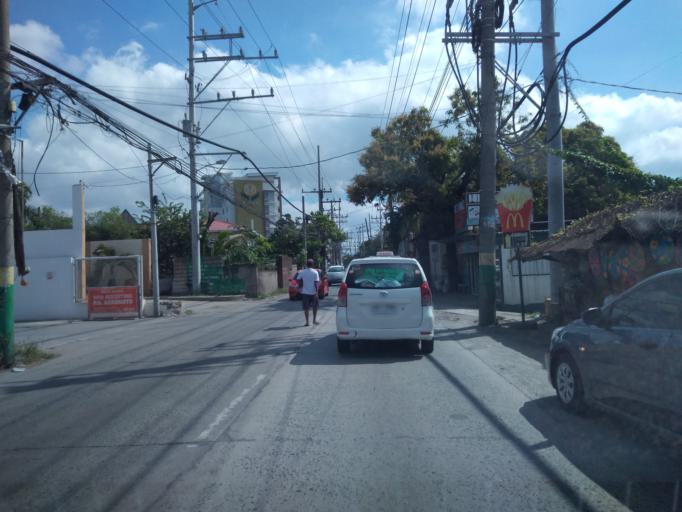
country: PH
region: Central Luzon
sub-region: Province of Bulacan
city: Bocaue
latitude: 14.8081
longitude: 120.9440
